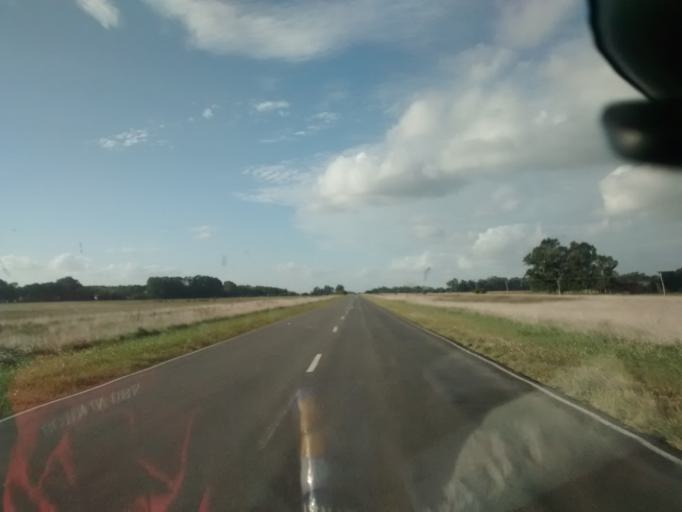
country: AR
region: Buenos Aires
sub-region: Partido de Ayacucho
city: Ayacucho
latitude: -36.6665
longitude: -58.5744
